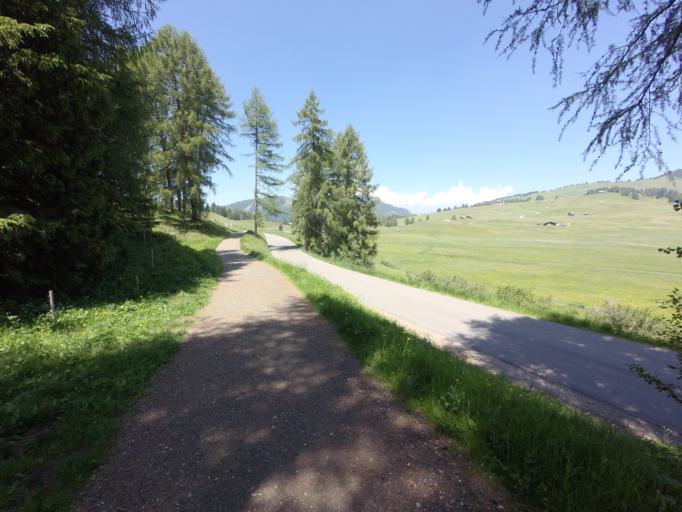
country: IT
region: Trentino-Alto Adige
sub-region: Bolzano
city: Ortisei
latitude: 46.5386
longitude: 11.6489
